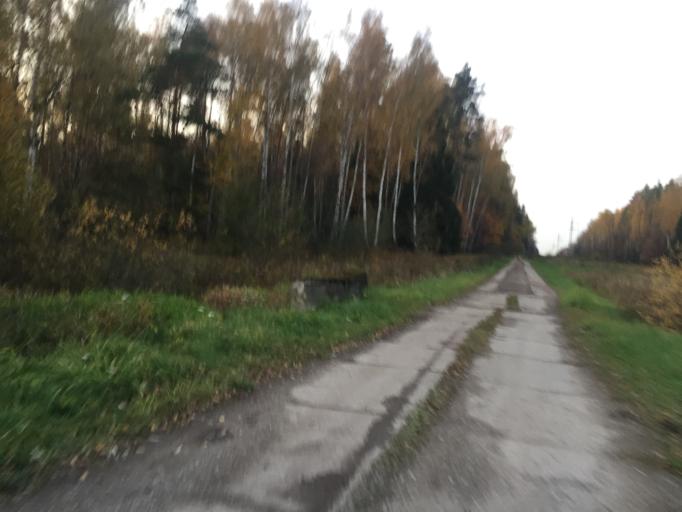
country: RU
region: Moskovskaya
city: Druzhba
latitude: 55.8644
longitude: 37.7679
